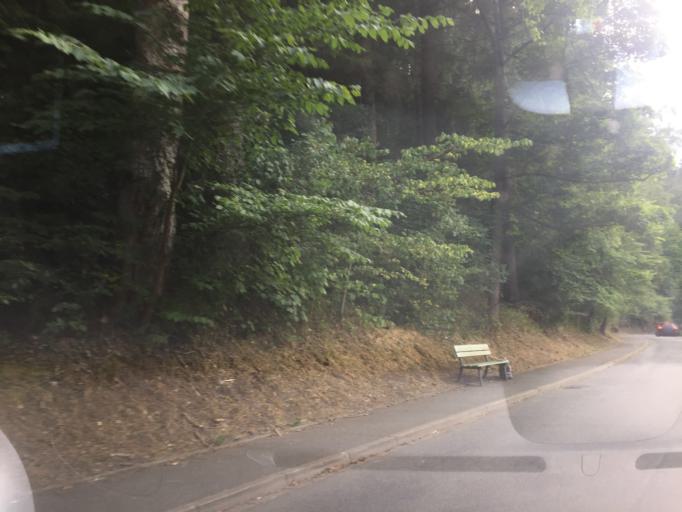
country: DE
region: Lower Saxony
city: Zorge
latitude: 51.6413
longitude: 10.6469
